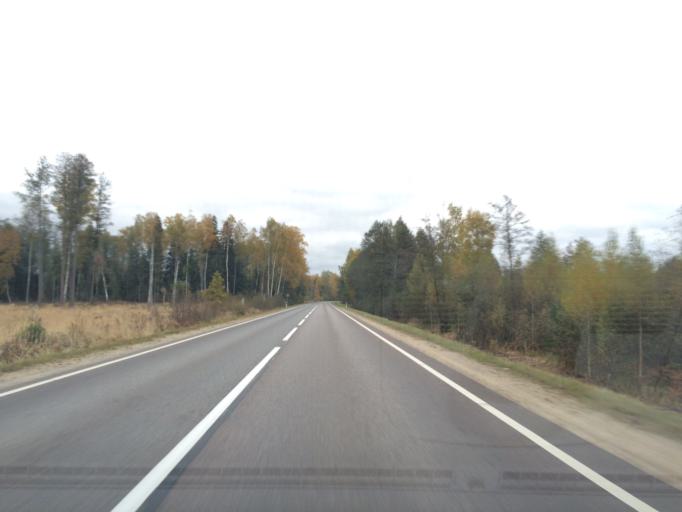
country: LV
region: Livani
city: Livani
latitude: 56.5272
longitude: 26.1961
